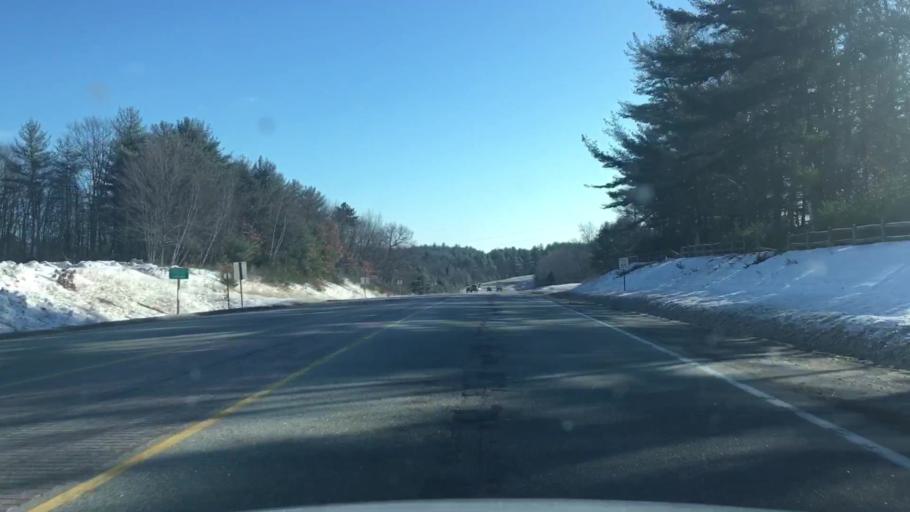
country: US
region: Maine
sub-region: Androscoggin County
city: Turner
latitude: 44.1845
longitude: -70.2352
